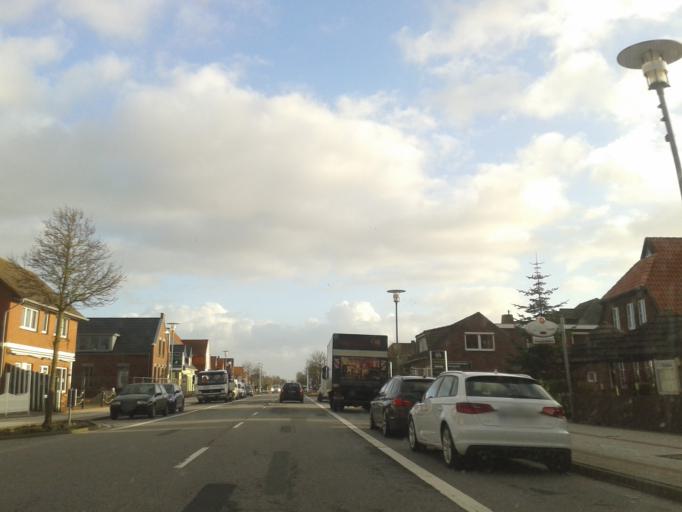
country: DE
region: Lower Saxony
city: Norddeich
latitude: 53.6184
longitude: 7.1596
